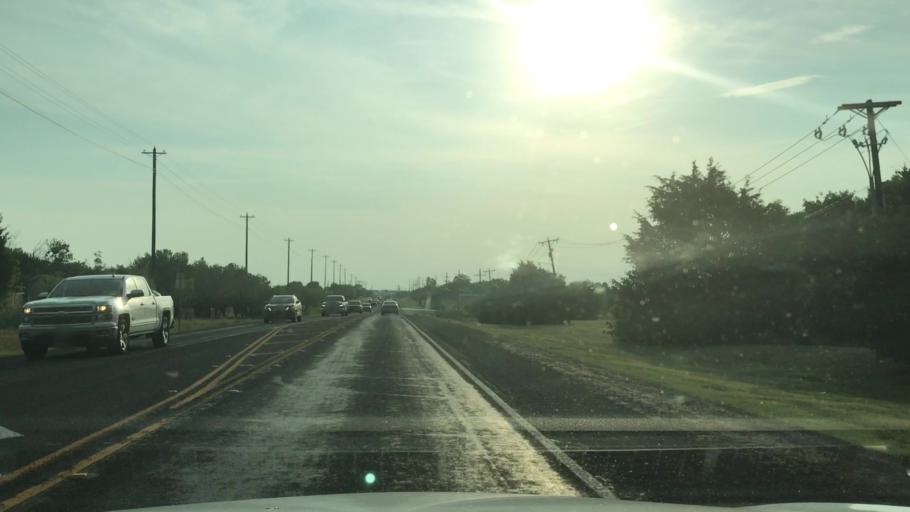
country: US
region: Texas
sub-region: Rockwall County
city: Rockwall
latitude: 32.9067
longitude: -96.4236
